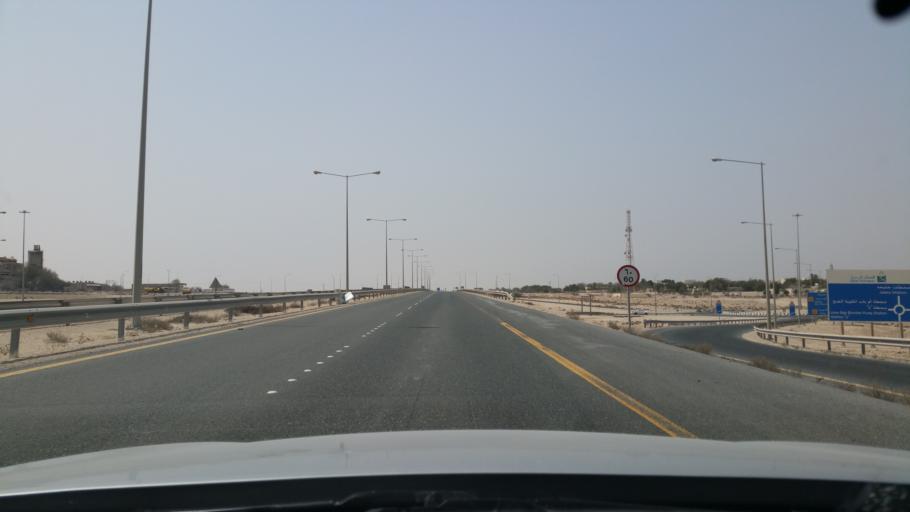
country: QA
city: Umm Bab
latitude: 25.2129
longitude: 50.8061
